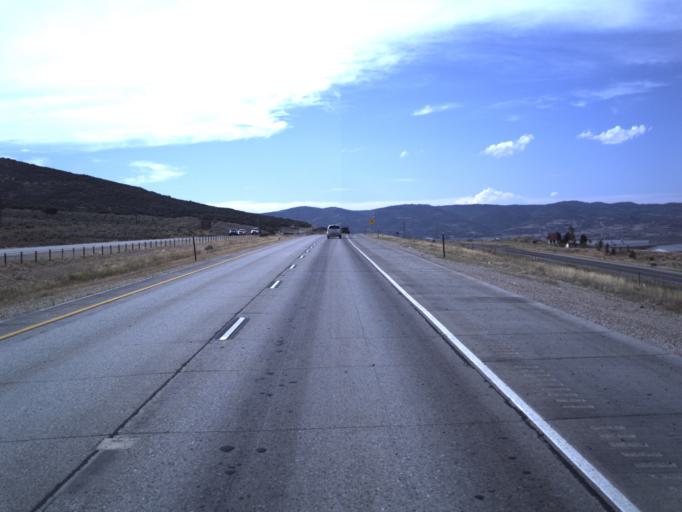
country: US
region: Utah
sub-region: Summit County
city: Park City
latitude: 40.6915
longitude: -111.4678
